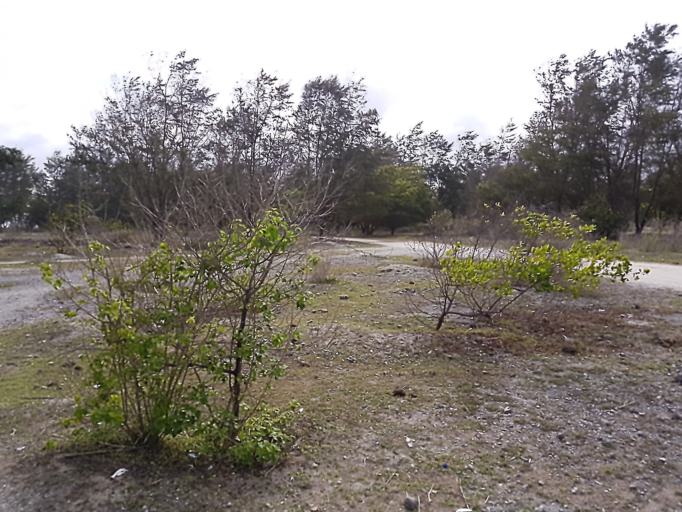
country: ID
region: Bali
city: Karyadharma
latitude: -8.7415
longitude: 115.2400
